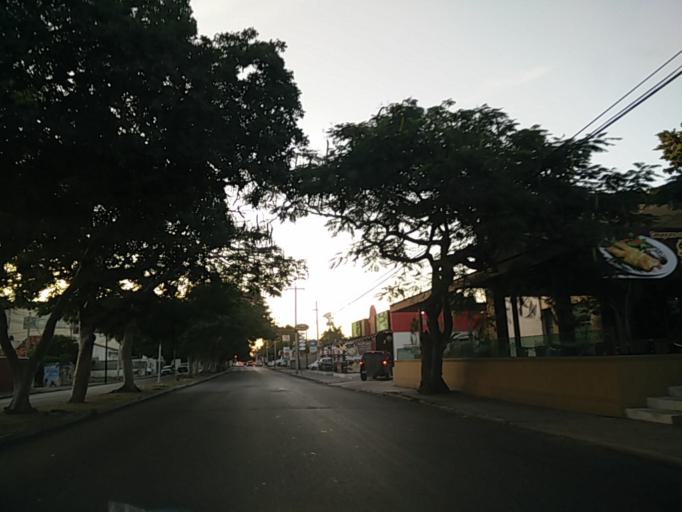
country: MX
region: Yucatan
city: Merida
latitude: 20.9975
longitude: -89.6080
